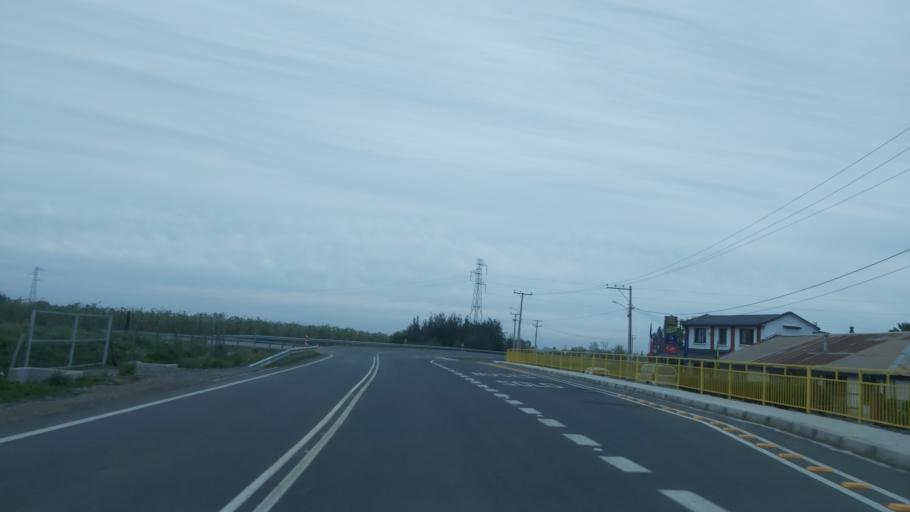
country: CL
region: Maule
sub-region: Provincia de Linares
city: Colbun
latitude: -35.6958
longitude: -71.4855
